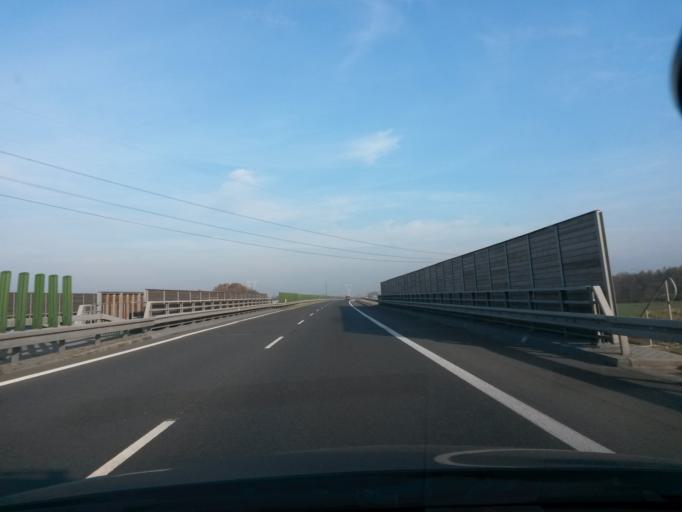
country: PL
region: Lower Silesian Voivodeship
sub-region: Powiat wroclawski
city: Dlugoleka
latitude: 51.2217
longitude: 17.1508
